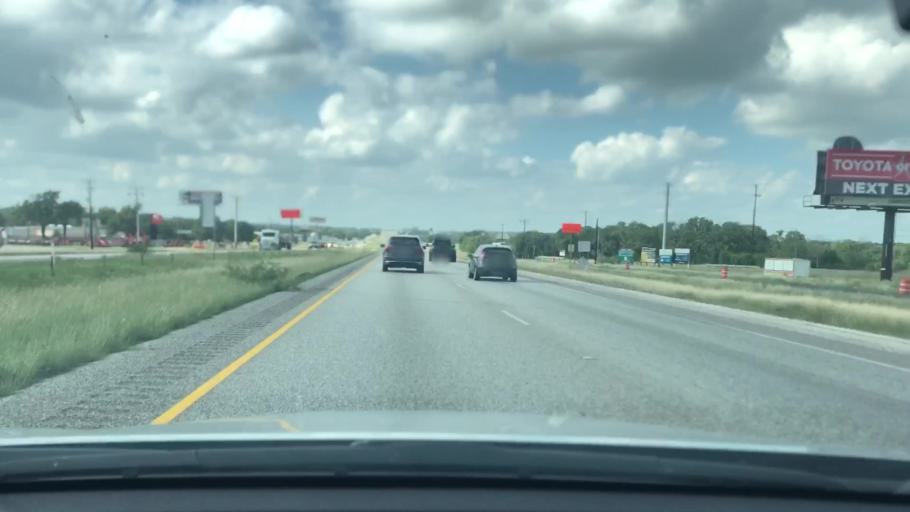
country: US
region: Texas
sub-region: Bexar County
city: Scenic Oaks
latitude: 29.7297
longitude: -98.6773
